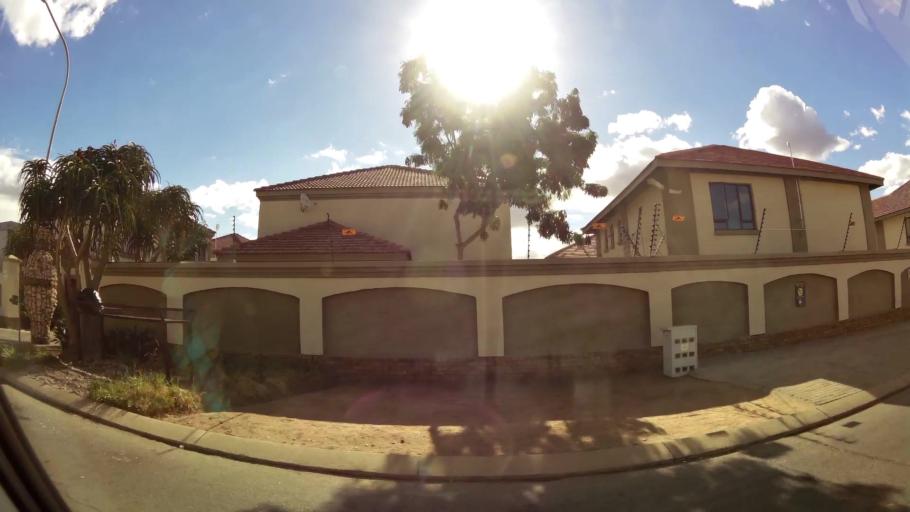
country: ZA
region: Limpopo
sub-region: Capricorn District Municipality
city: Polokwane
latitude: -23.8751
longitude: 29.4832
